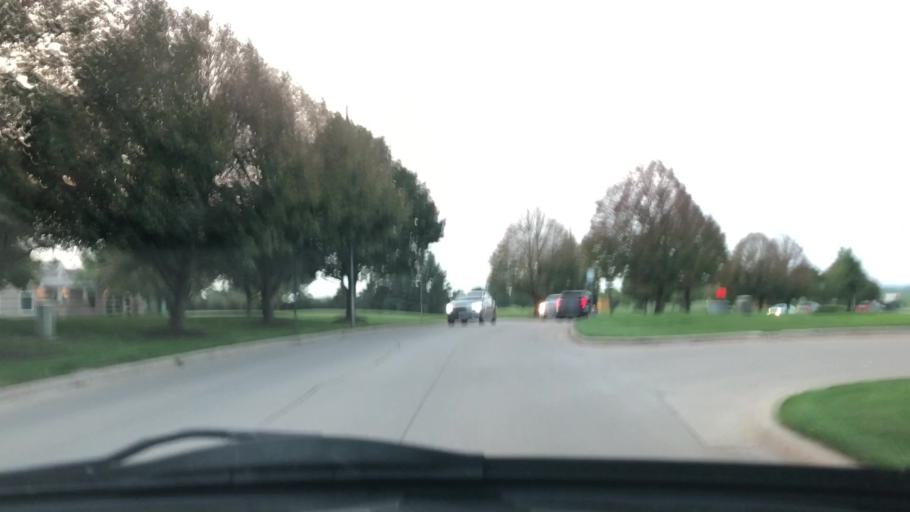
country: US
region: Iowa
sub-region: Johnson County
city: North Liberty
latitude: 41.7130
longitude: -91.6054
